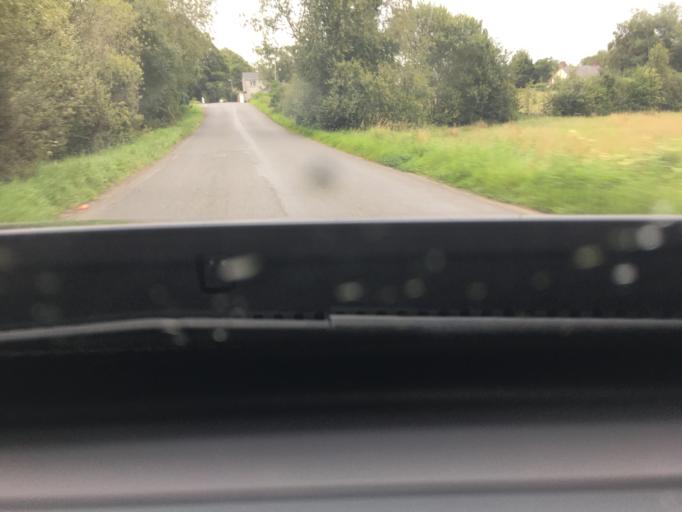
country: GB
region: Northern Ireland
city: Moy
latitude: 54.5159
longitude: -6.6312
